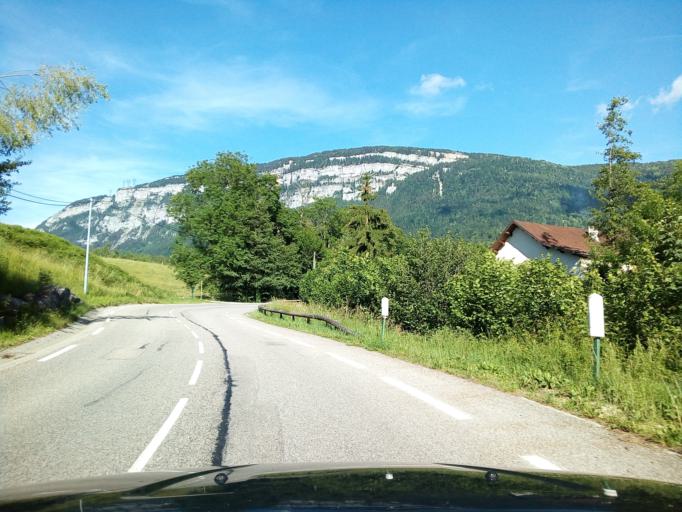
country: FR
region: Rhone-Alpes
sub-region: Departement de la Savoie
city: La Bridoire
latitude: 45.5128
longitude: 5.7696
